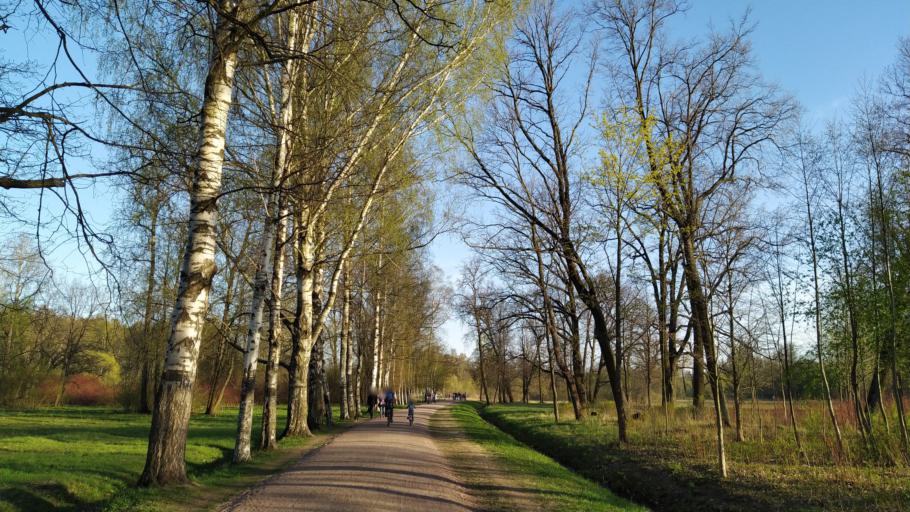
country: RU
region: St.-Petersburg
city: Pavlovsk
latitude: 59.7081
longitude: 30.4246
